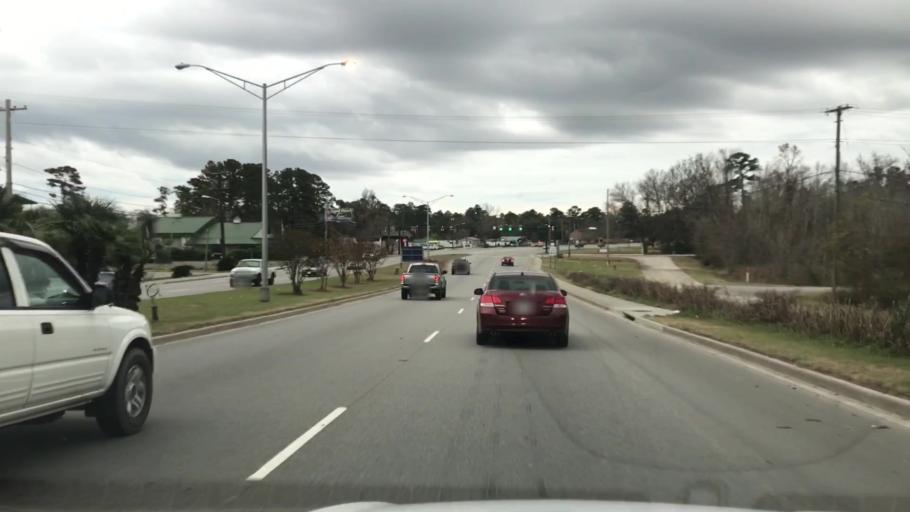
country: US
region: South Carolina
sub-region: Georgetown County
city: Georgetown
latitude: 33.3540
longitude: -79.2933
